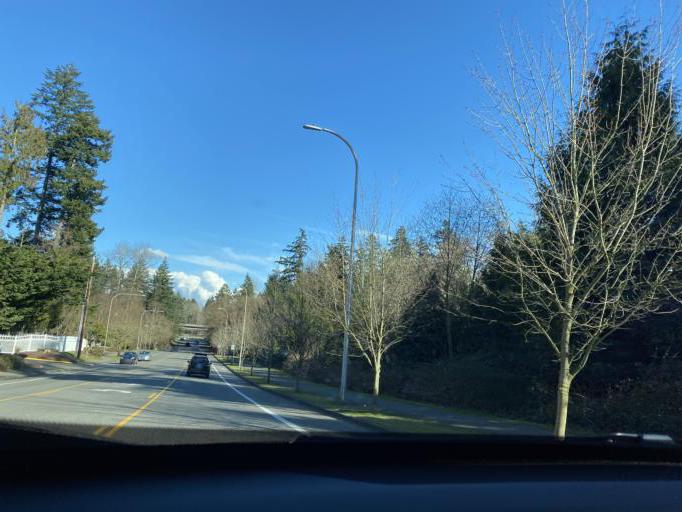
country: US
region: Washington
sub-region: King County
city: Federal Way
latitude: 47.3006
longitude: -122.3065
